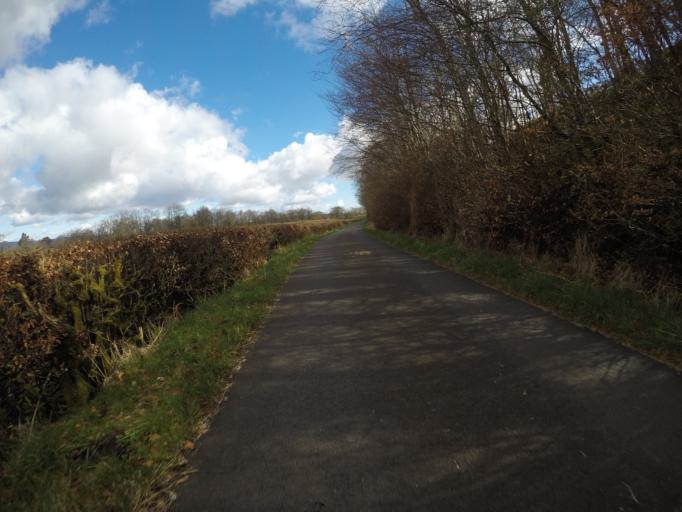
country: GB
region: Scotland
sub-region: North Ayrshire
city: Beith
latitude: 55.7144
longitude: -4.6456
